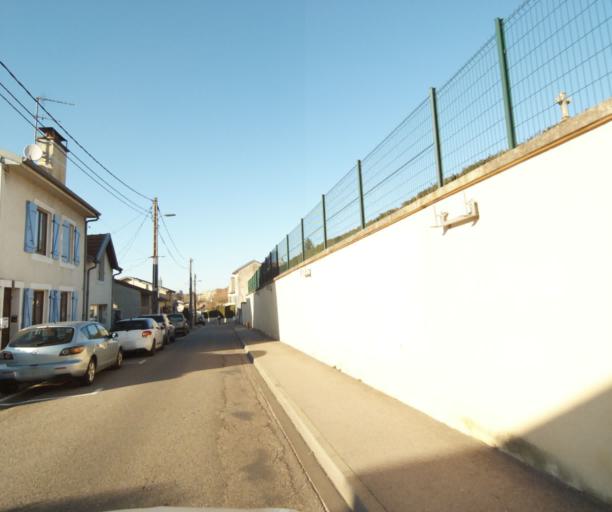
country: FR
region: Lorraine
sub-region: Departement de Meurthe-et-Moselle
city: Malzeville
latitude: 48.7134
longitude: 6.1857
